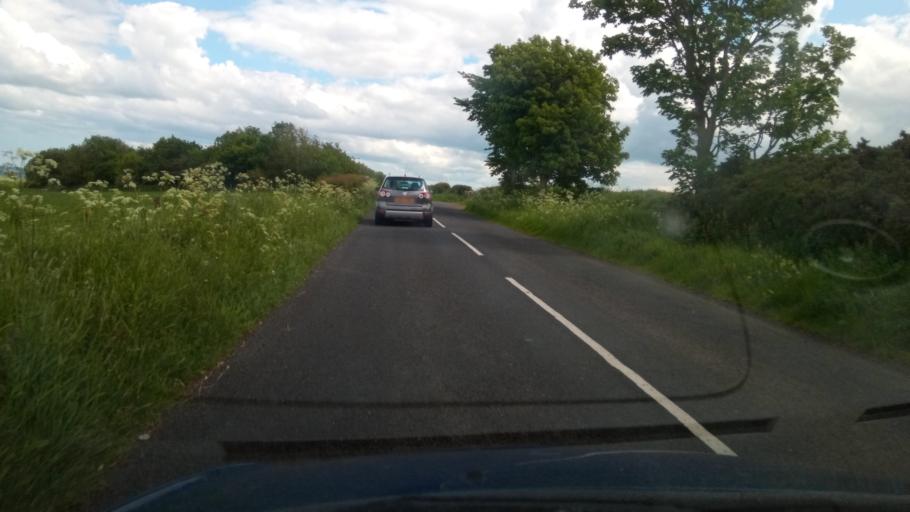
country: GB
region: Scotland
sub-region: The Scottish Borders
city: Coldstream
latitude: 55.6041
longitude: -2.2671
